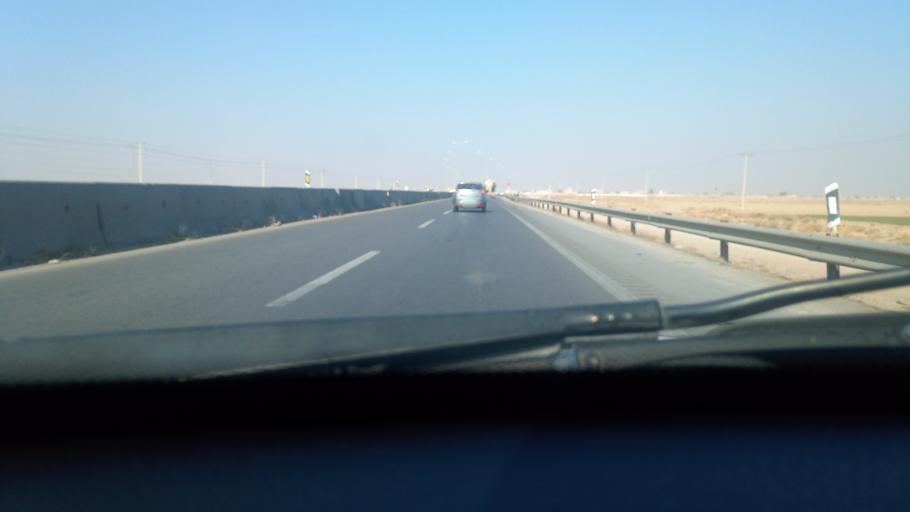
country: IR
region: Razavi Khorasan
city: Chenaran
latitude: 36.8053
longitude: 58.8518
